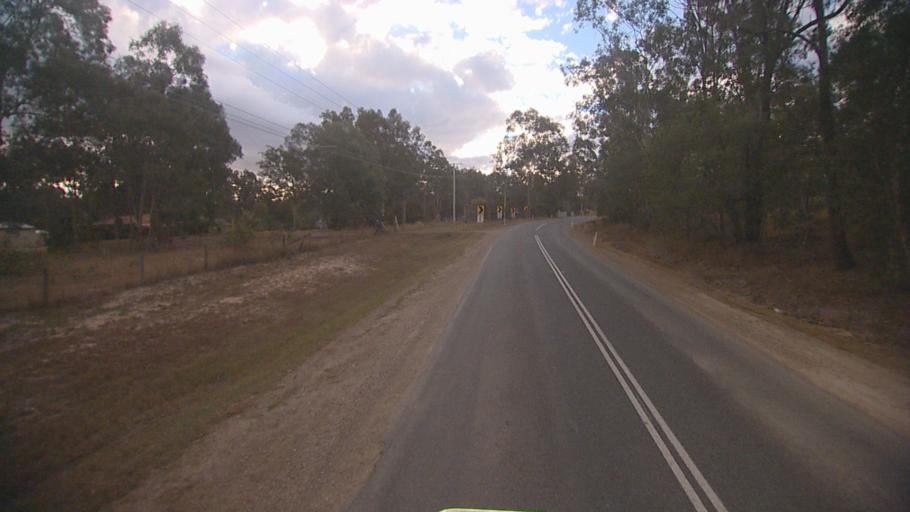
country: AU
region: Queensland
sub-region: Logan
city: Cedar Vale
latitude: -27.8451
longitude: 153.0491
